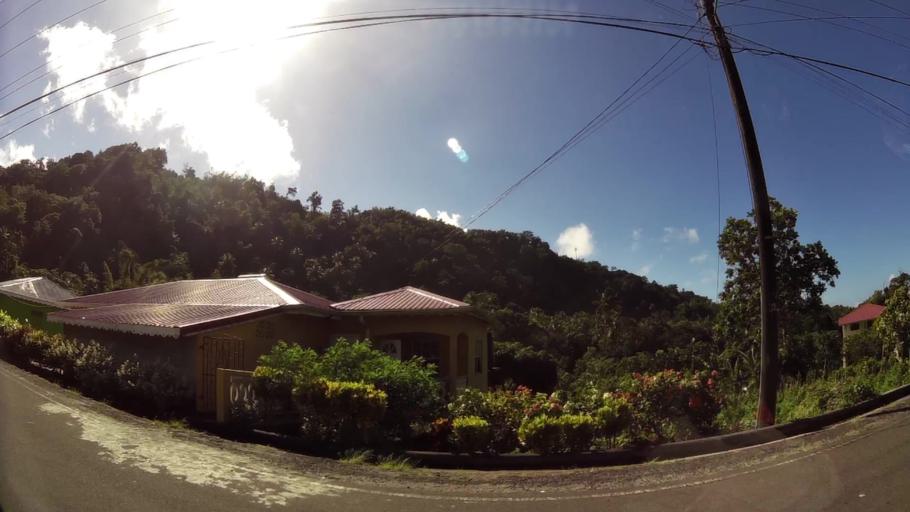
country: LC
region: Soufriere
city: Soufriere
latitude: 13.8189
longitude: -61.0377
